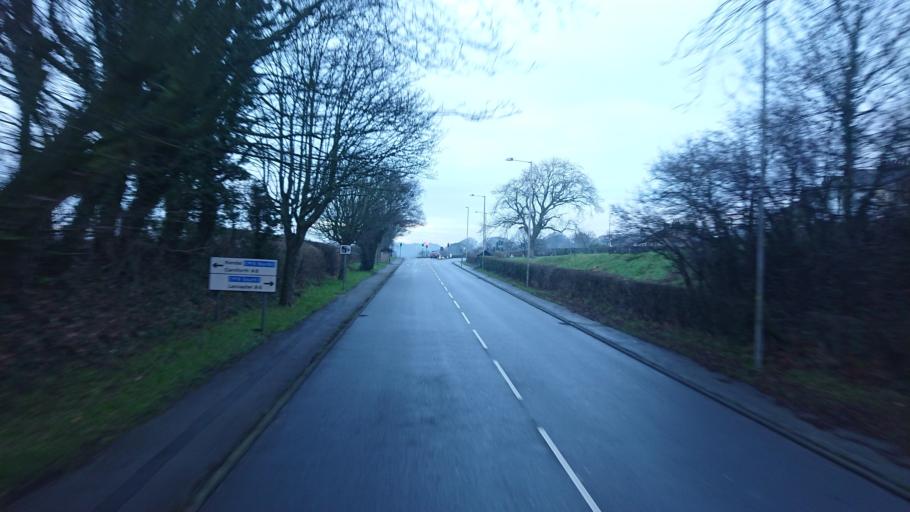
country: GB
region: England
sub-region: Lancashire
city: Bolton le Sands
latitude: 54.0996
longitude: -2.7979
